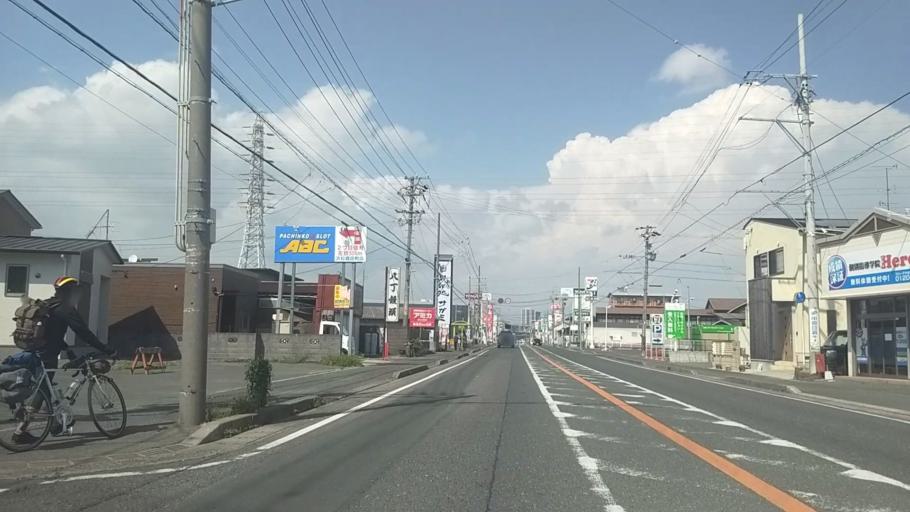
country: JP
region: Shizuoka
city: Hamamatsu
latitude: 34.6896
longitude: 137.7141
